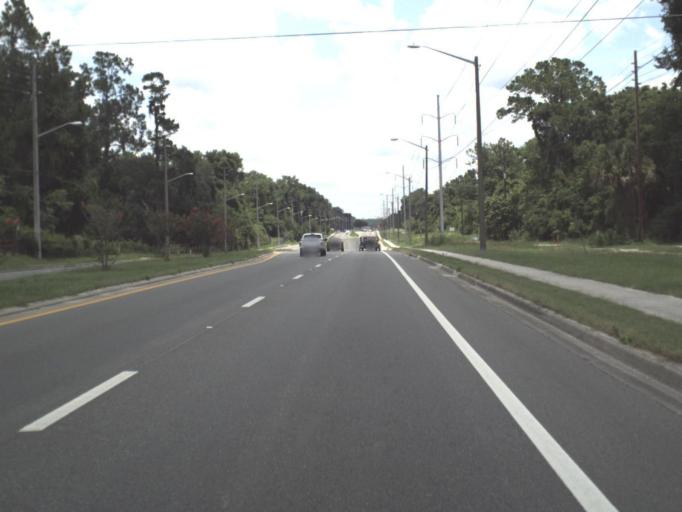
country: US
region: Florida
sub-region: Alachua County
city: Gainesville
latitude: 29.6094
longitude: -82.4012
